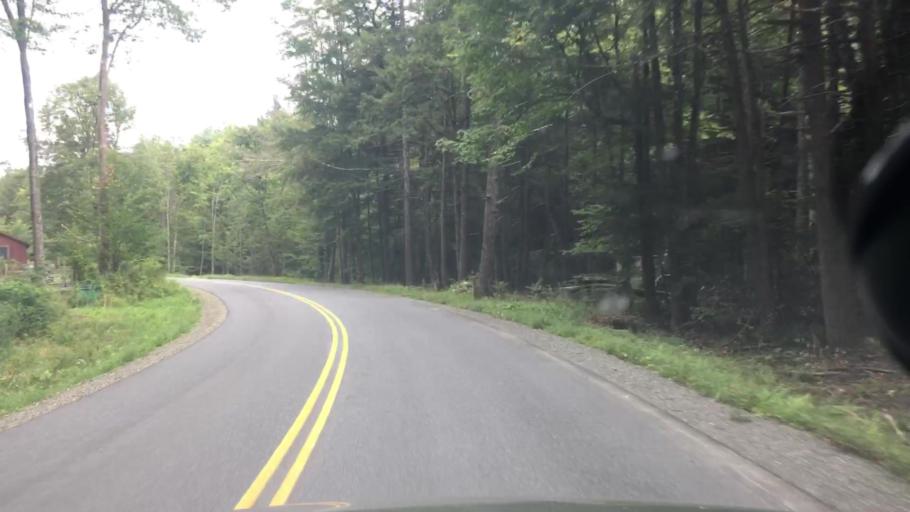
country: US
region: Massachusetts
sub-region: Franklin County
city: Colrain
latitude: 42.7647
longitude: -72.7645
